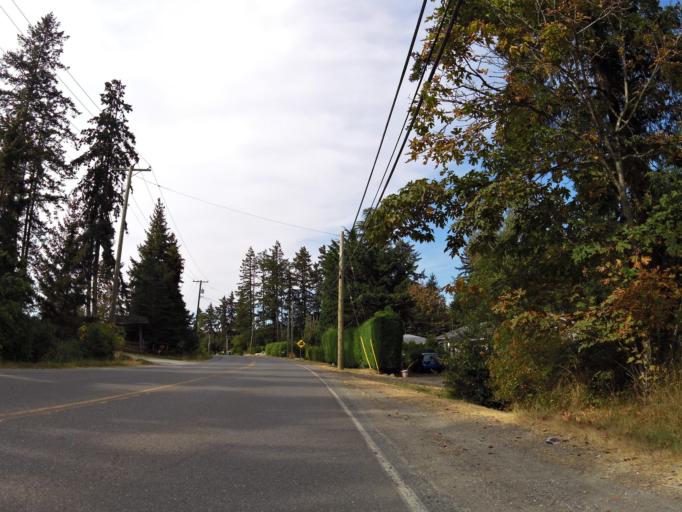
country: CA
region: British Columbia
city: Duncan
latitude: 48.7327
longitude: -123.6088
